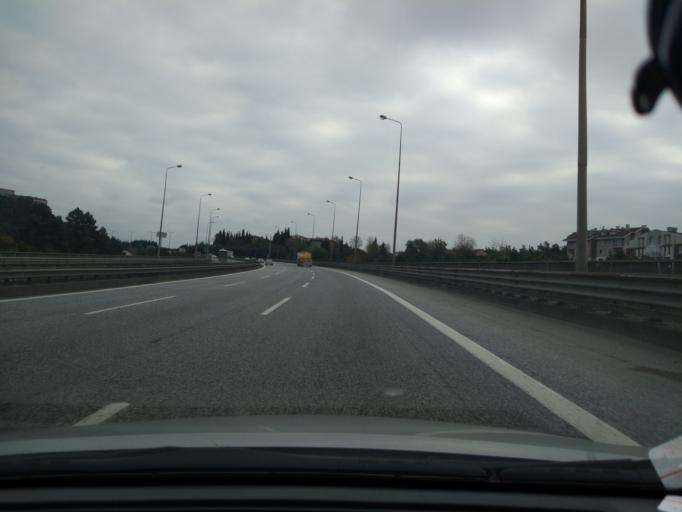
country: TR
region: Kocaeli
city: Derince
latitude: 40.7655
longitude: 29.8590
